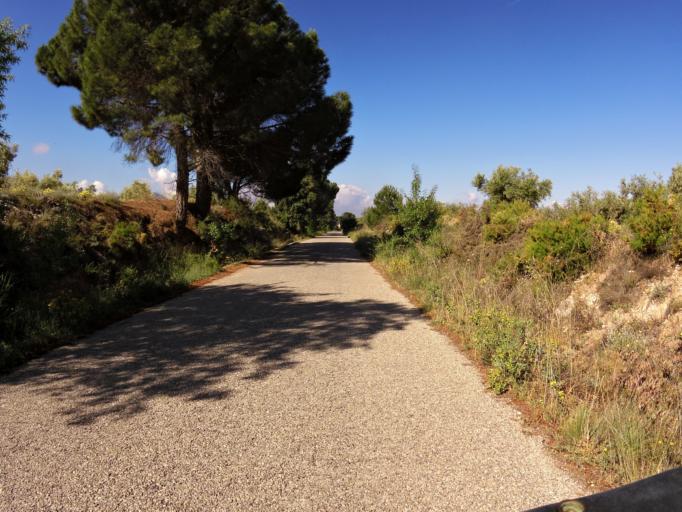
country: ES
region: Valencia
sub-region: Provincia de Alicante
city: Biar
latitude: 38.6347
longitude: -0.7859
